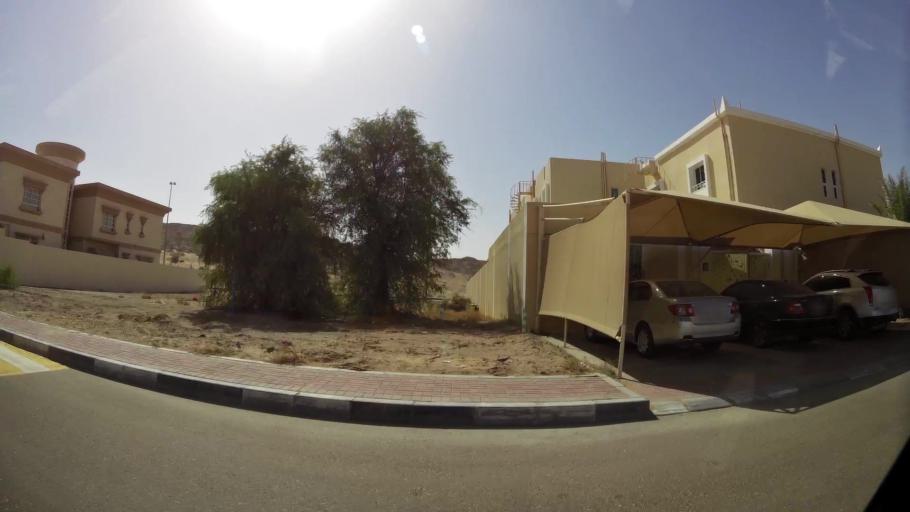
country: OM
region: Al Buraimi
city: Al Buraymi
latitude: 24.3194
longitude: 55.8128
